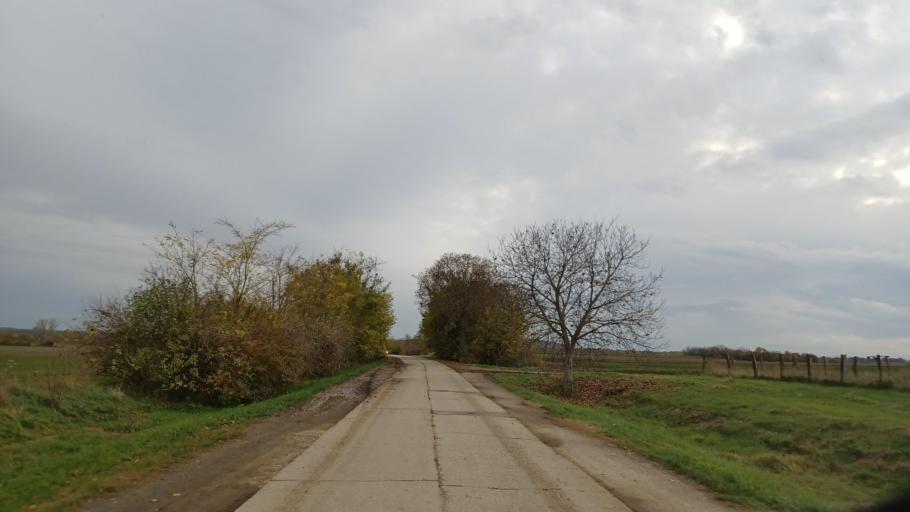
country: HU
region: Tolna
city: Nagydorog
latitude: 46.6365
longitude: 18.6051
